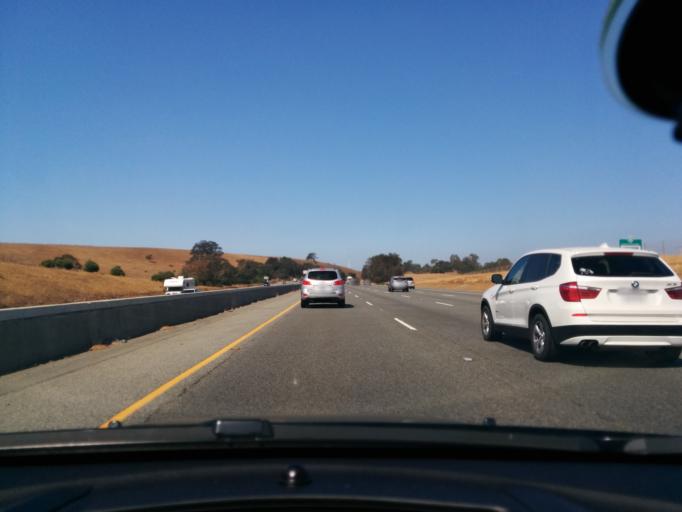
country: US
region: California
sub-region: San Mateo County
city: Ladera
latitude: 37.4117
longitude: -122.2025
